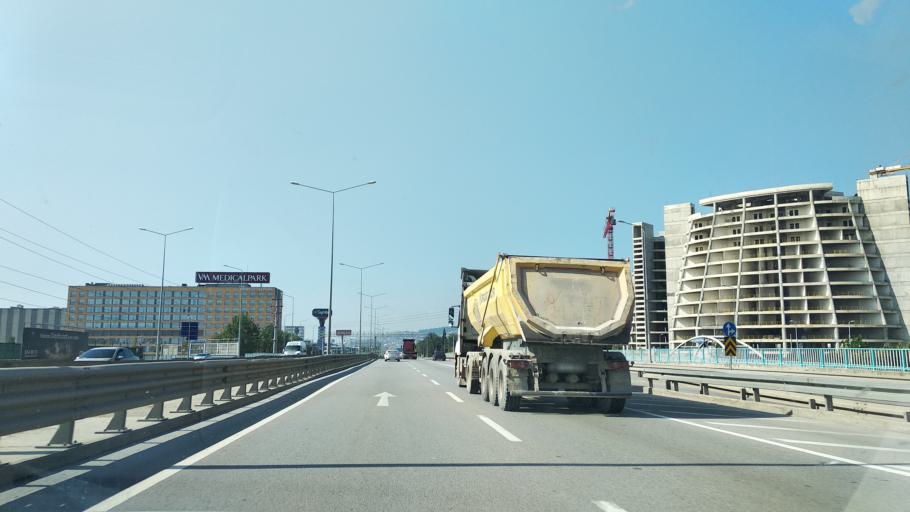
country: TR
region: Kocaeli
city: Kosekoy
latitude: 40.7590
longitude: 29.9851
